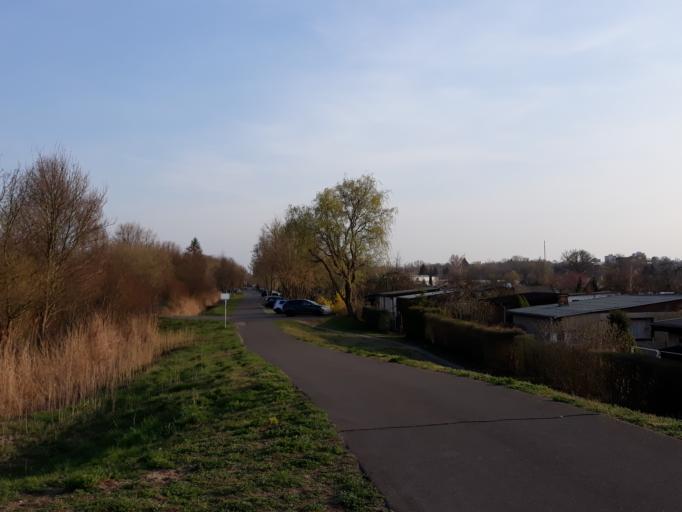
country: DE
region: Brandenburg
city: Frankfurt (Oder)
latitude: 52.3693
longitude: 14.5437
